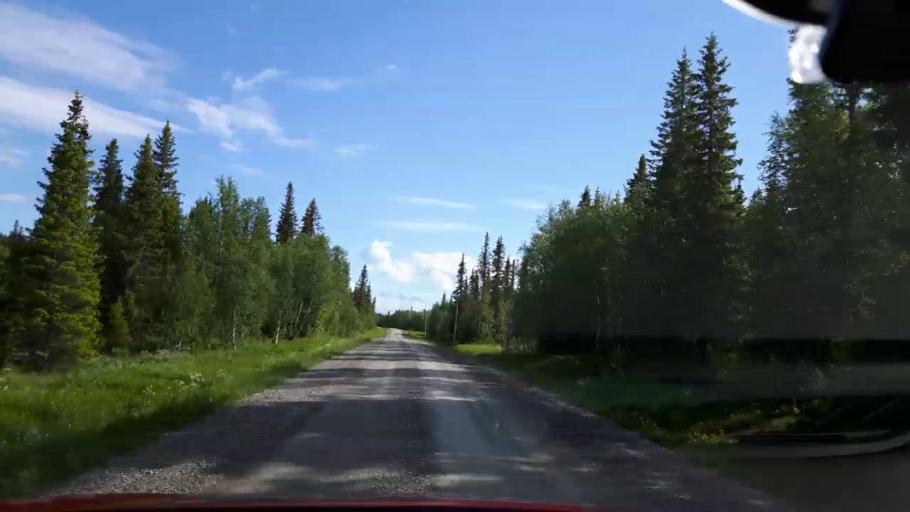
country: SE
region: Jaemtland
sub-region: Krokoms Kommun
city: Valla
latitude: 63.7920
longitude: 14.0465
